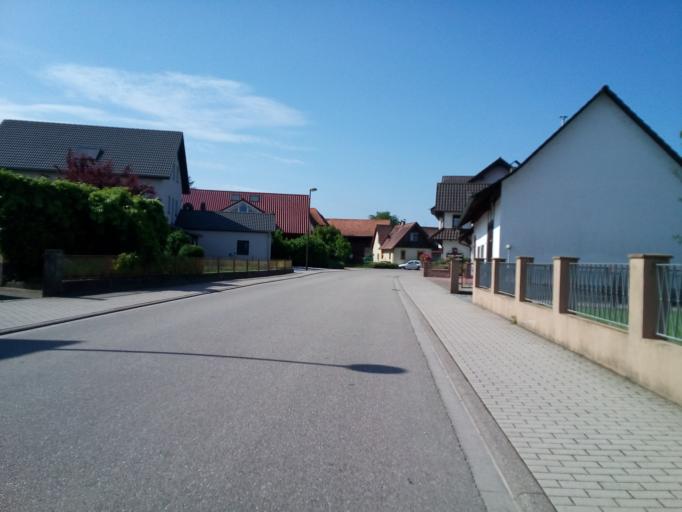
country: DE
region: Baden-Wuerttemberg
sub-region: Freiburg Region
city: Rheinau
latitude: 48.6283
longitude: 7.9212
